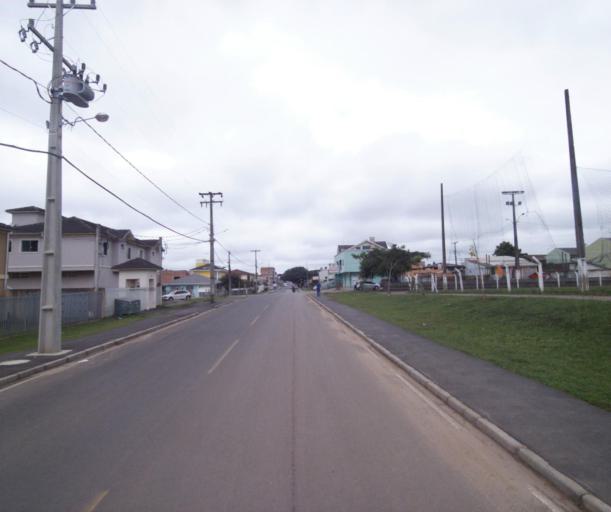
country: BR
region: Parana
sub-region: Quatro Barras
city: Quatro Barras
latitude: -25.3611
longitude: -49.1026
